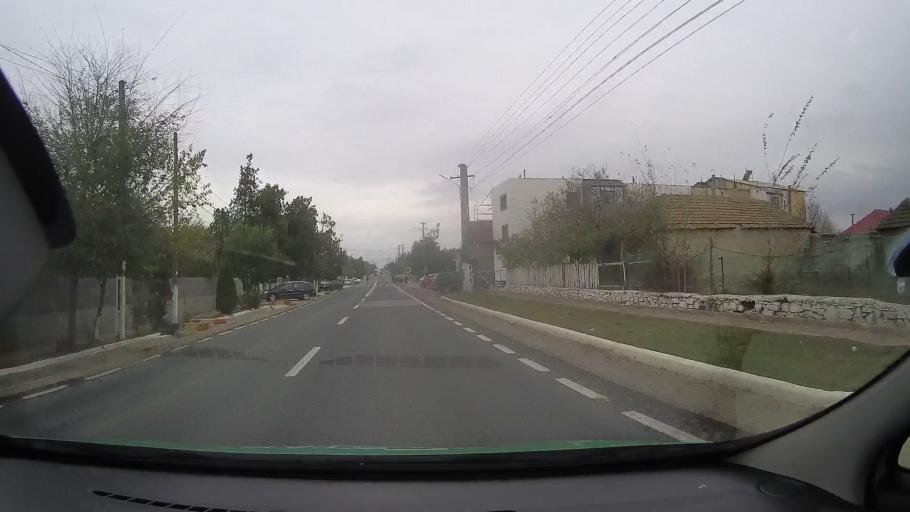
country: RO
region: Constanta
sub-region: Comuna Nicolae Balcescu
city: Nicolae Balcescu
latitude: 44.3886
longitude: 28.3765
